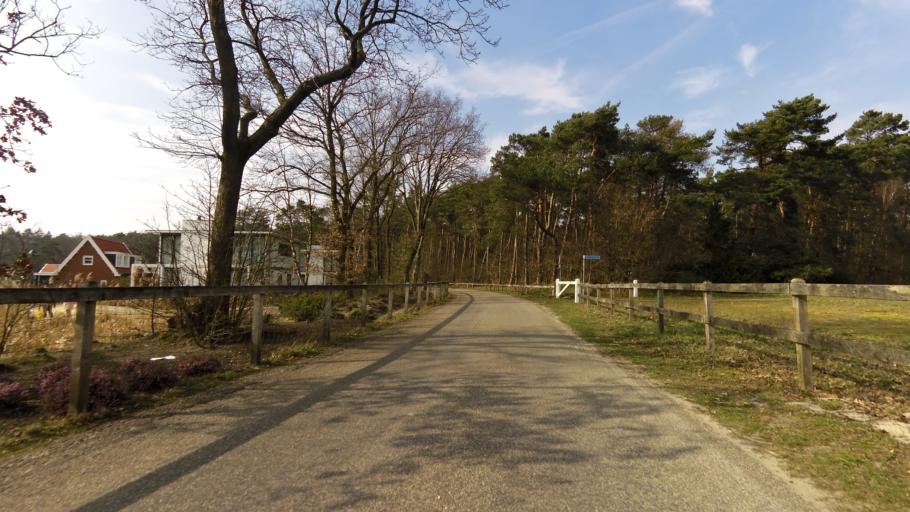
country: NL
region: Gelderland
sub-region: Gemeente Ede
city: Otterlo
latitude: 52.0935
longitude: 5.7811
